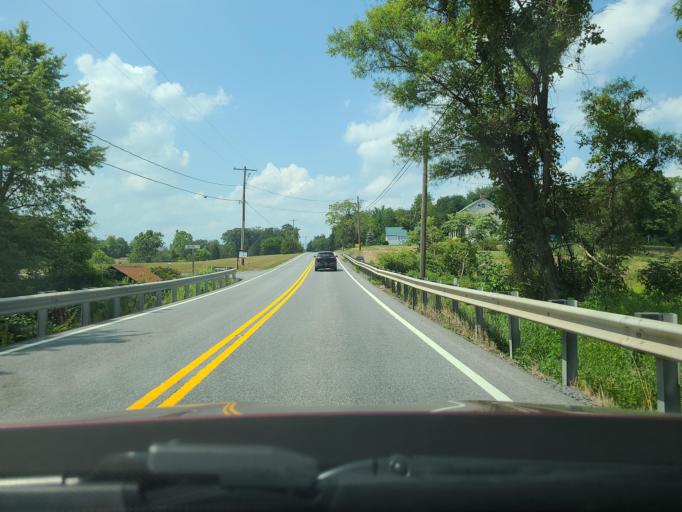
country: US
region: Maryland
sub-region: Frederick County
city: Woodsboro
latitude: 39.5116
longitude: -77.2818
